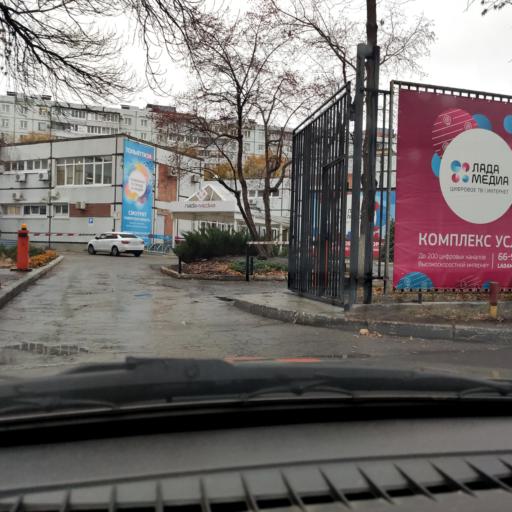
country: RU
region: Samara
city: Tol'yatti
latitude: 53.5214
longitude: 49.2878
